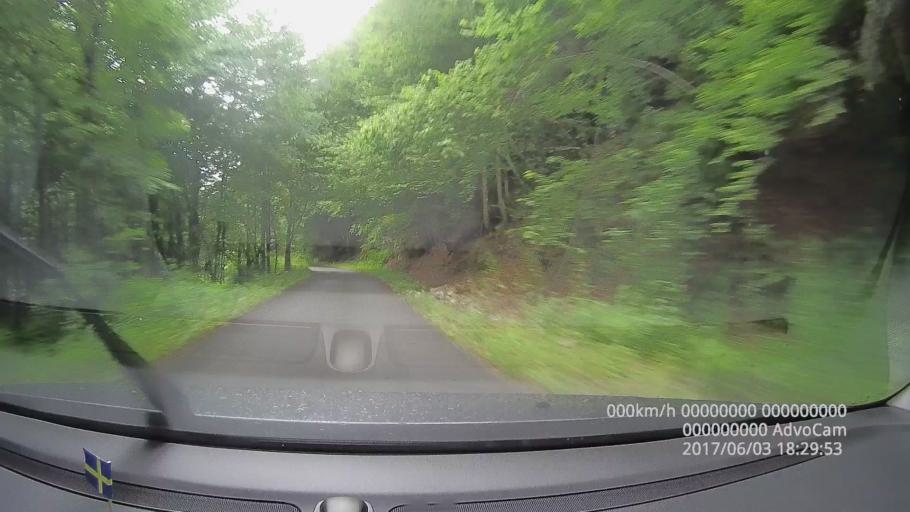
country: RO
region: Gorj
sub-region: Comuna Runcu
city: Dobrita
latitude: 45.1493
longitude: 23.2046
